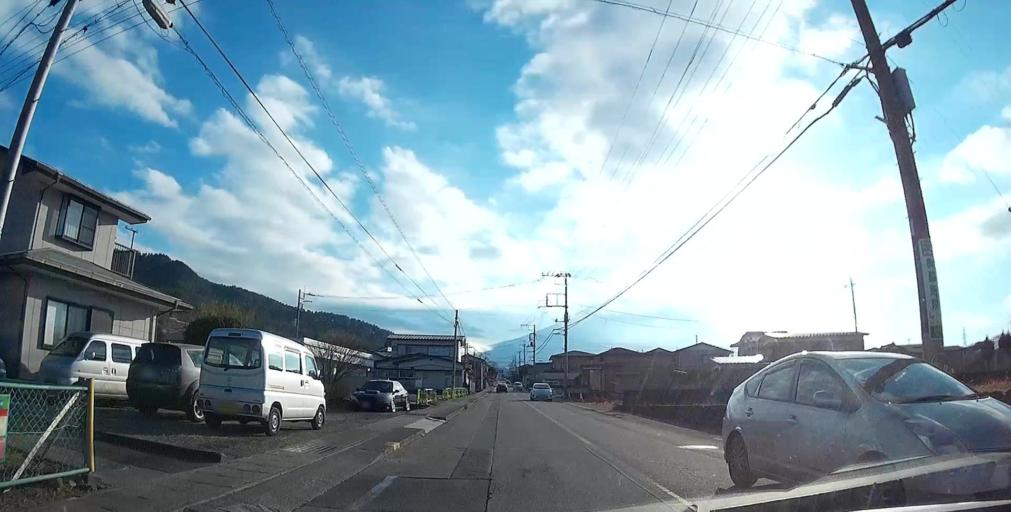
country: JP
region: Yamanashi
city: Fujikawaguchiko
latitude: 35.4822
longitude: 138.8179
